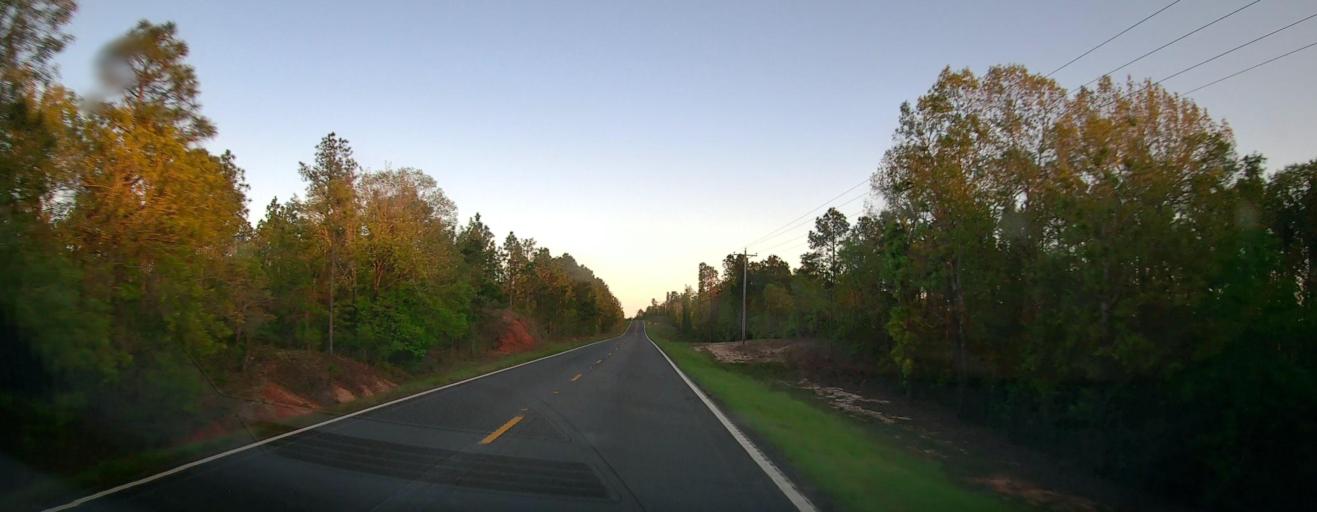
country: US
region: Georgia
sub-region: Marion County
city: Buena Vista
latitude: 32.4092
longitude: -84.5833
